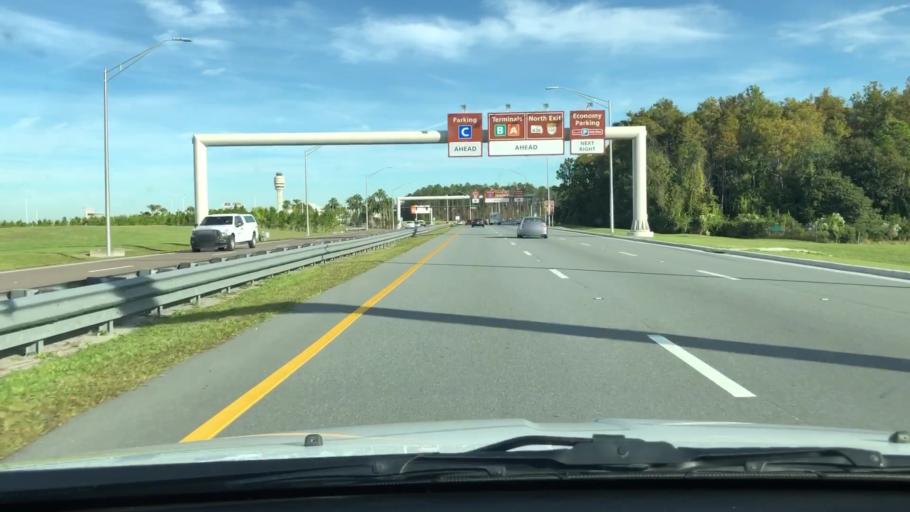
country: US
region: Florida
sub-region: Orange County
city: Taft
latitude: 28.4123
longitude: -81.3040
